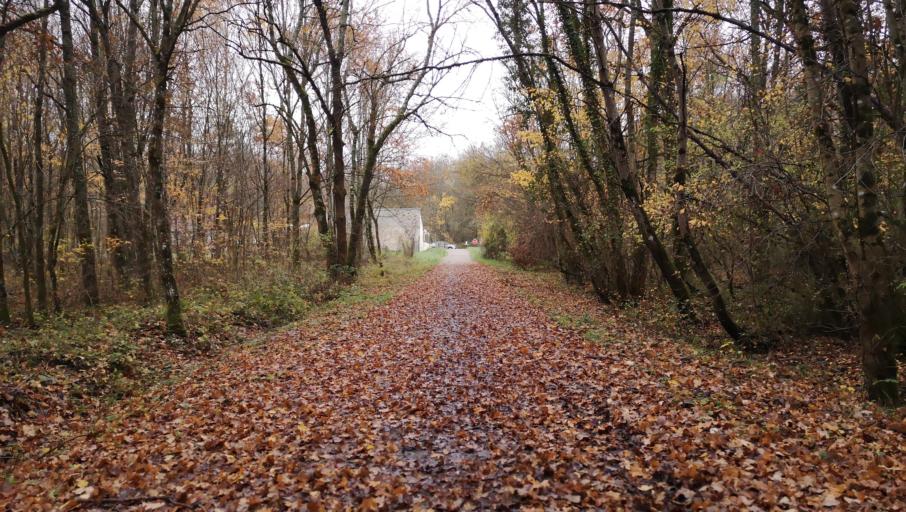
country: FR
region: Centre
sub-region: Departement du Loiret
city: Saint-Jean-de-Braye
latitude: 47.9329
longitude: 1.9864
